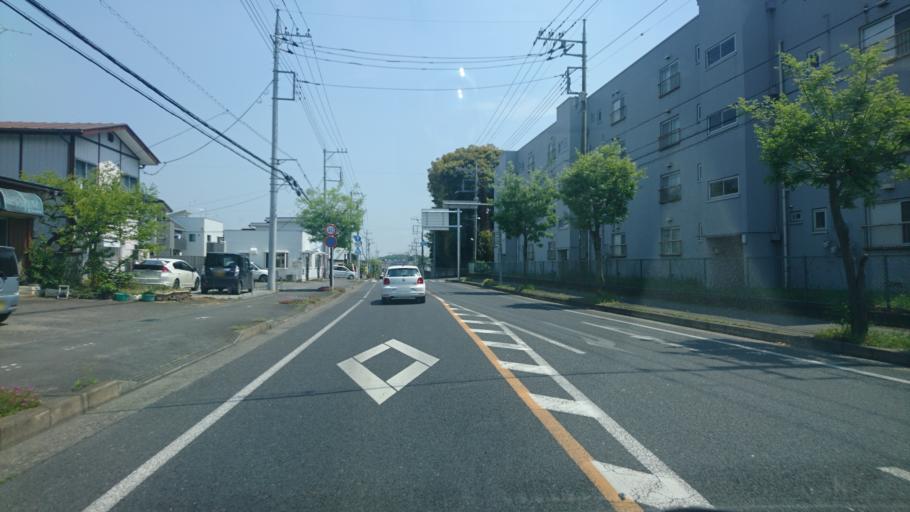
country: JP
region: Tochigi
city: Oyama
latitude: 36.3090
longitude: 139.8339
